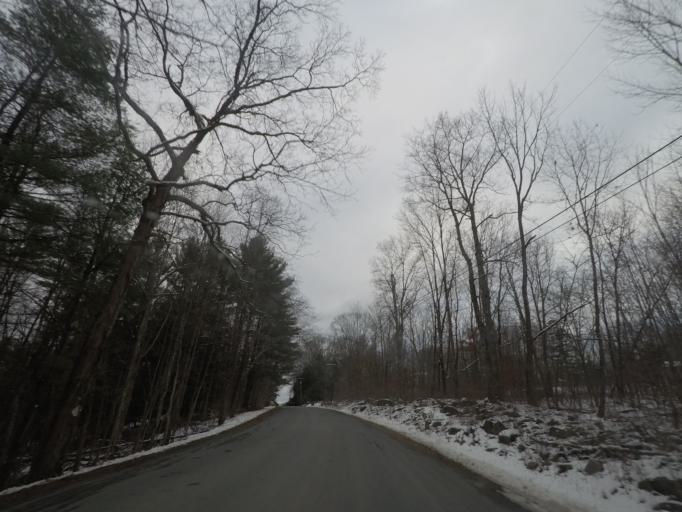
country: US
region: New York
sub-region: Rensselaer County
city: Averill Park
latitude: 42.6428
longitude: -73.5386
